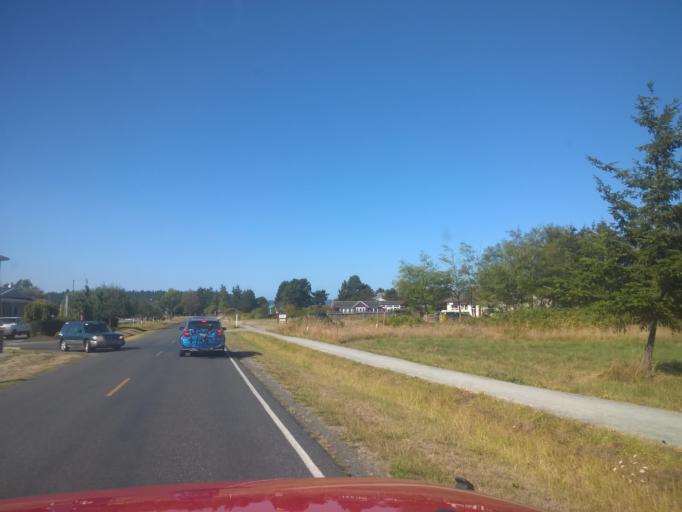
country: US
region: Washington
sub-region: San Juan County
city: Friday Harbor
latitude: 48.5266
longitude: -122.9123
